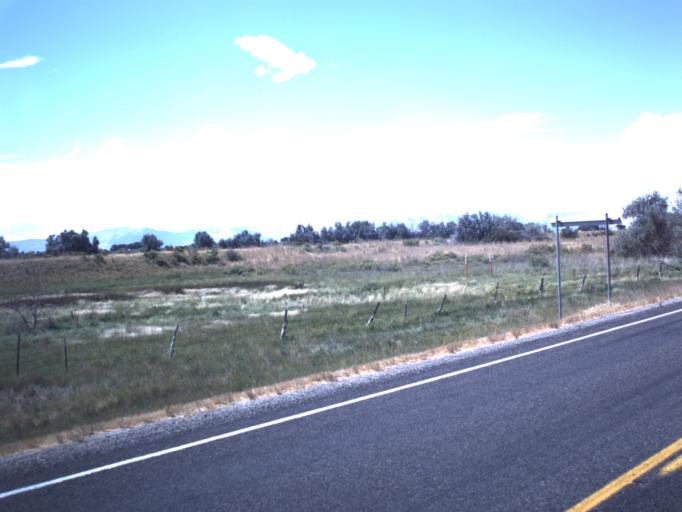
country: US
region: Utah
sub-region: Box Elder County
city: Honeyville
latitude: 41.5654
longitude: -112.1785
